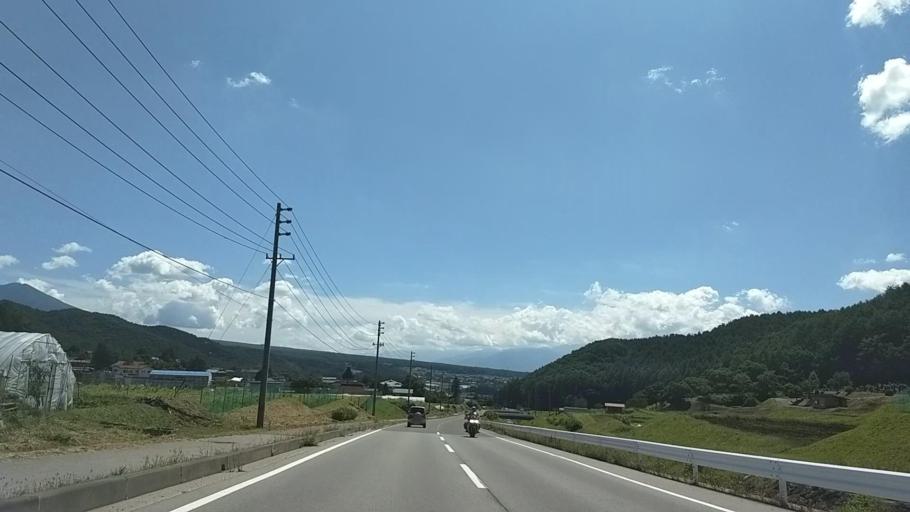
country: JP
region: Nagano
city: Chino
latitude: 36.0585
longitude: 138.2239
